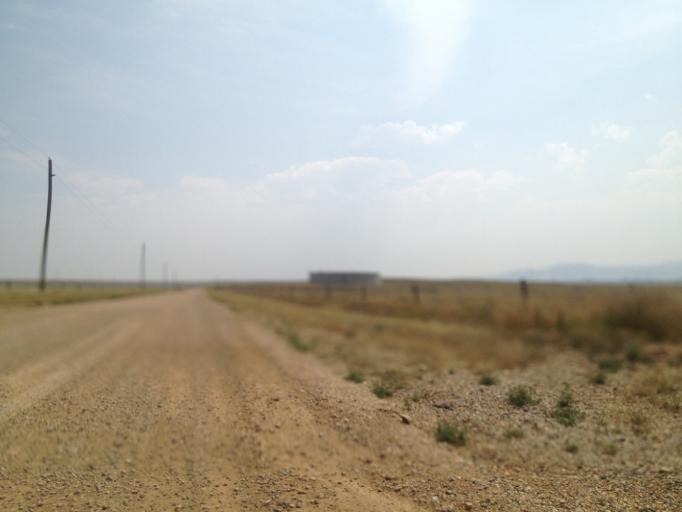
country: US
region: Colorado
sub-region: Boulder County
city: Superior
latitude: 39.9432
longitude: -105.1988
